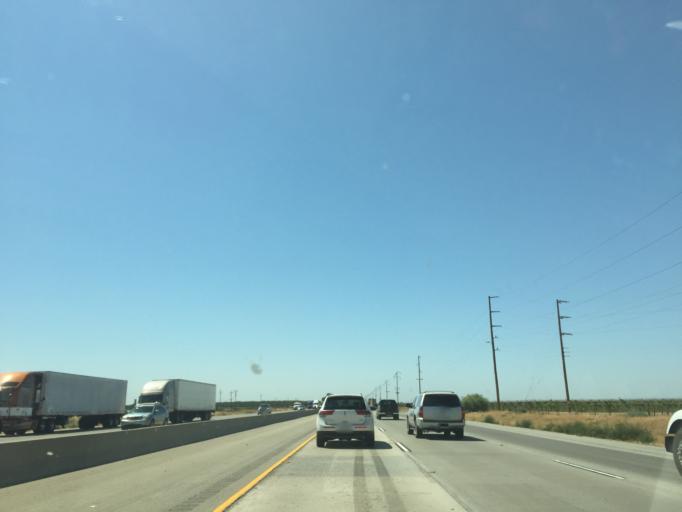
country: US
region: California
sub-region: Kern County
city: Greenacres
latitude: 35.4695
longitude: -119.1243
